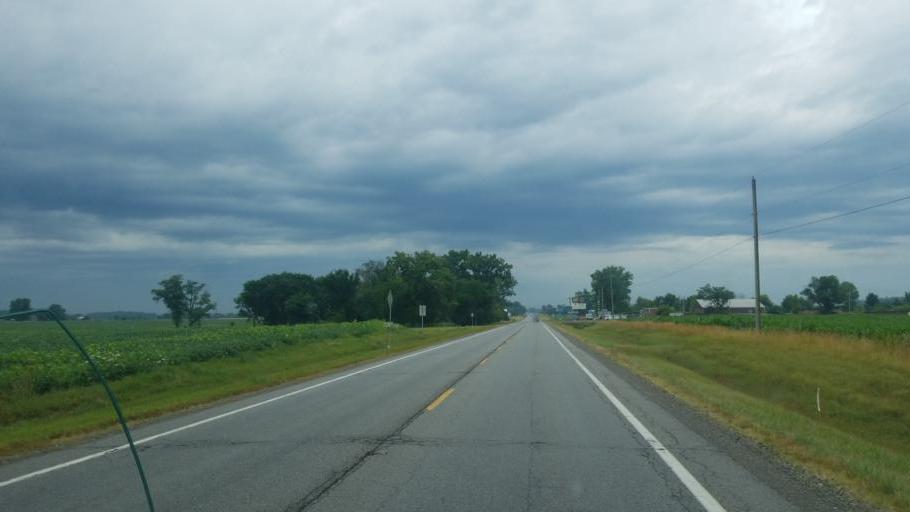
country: US
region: Ohio
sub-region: Williams County
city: Edgerton
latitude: 41.4480
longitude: -84.7134
